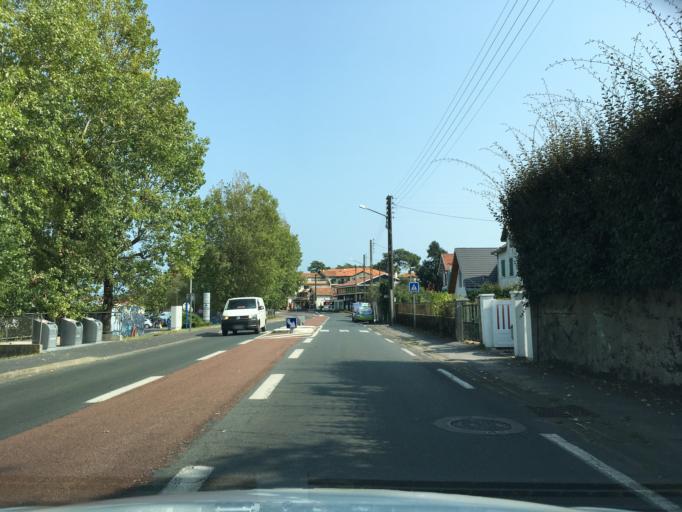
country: FR
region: Aquitaine
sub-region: Departement des Pyrenees-Atlantiques
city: Boucau
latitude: 43.5251
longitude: -1.5088
